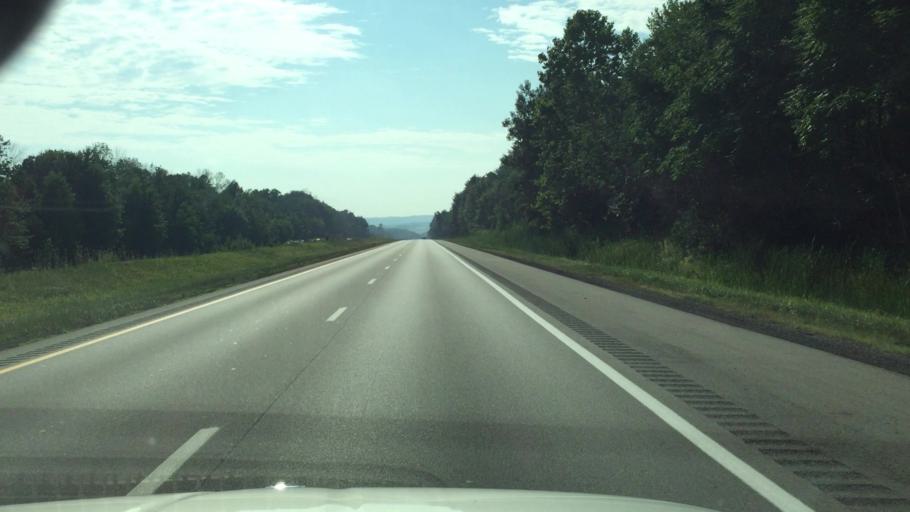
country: US
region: Ohio
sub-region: Muskingum County
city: Zanesville
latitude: 39.9508
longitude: -82.1724
